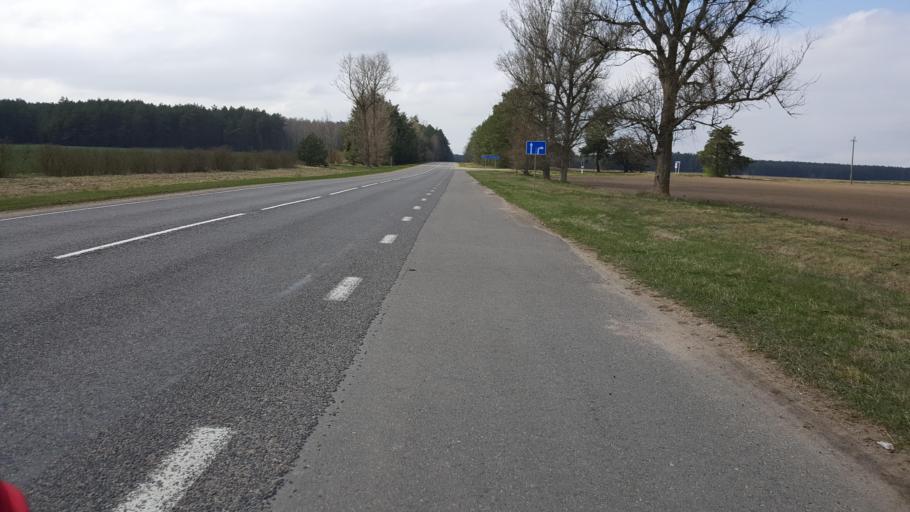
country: BY
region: Brest
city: Kamyanyets
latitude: 52.3737
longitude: 23.8789
